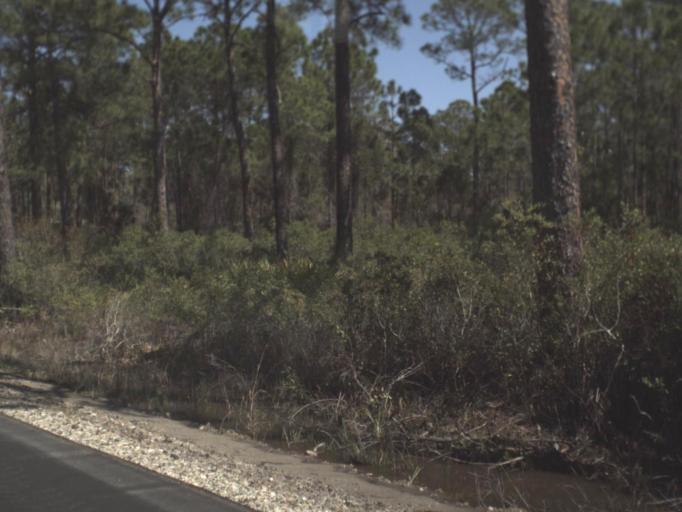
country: US
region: Florida
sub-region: Gulf County
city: Port Saint Joe
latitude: 29.6955
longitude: -85.3077
